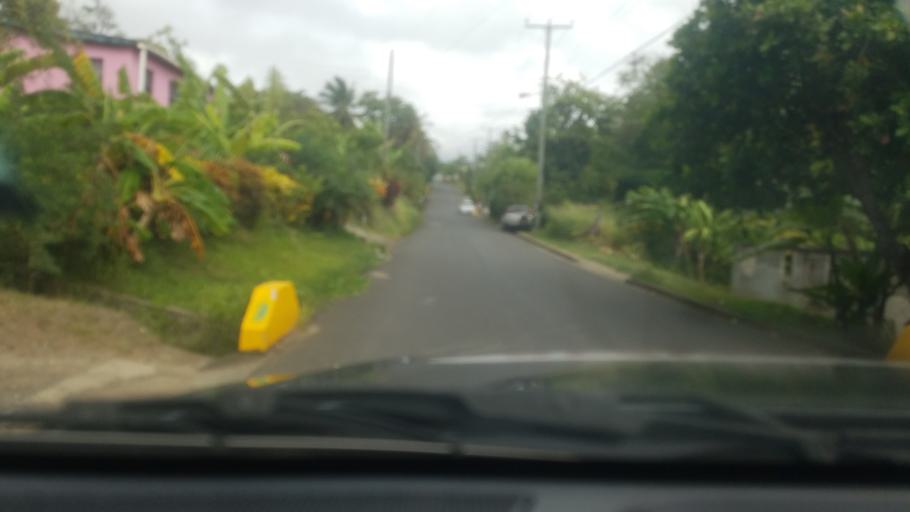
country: LC
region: Micoud Quarter
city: Micoud
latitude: 13.7978
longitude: -60.9174
